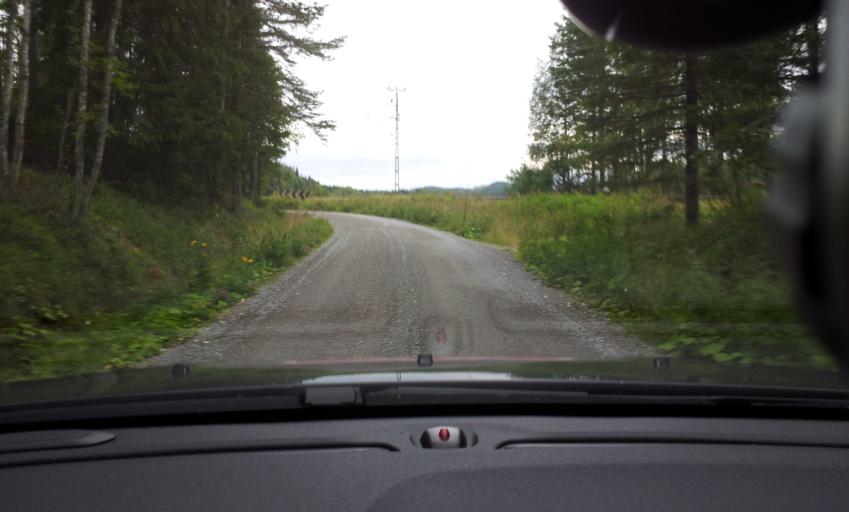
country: SE
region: Jaemtland
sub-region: OEstersunds Kommun
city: Brunflo
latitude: 62.9978
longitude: 14.9646
